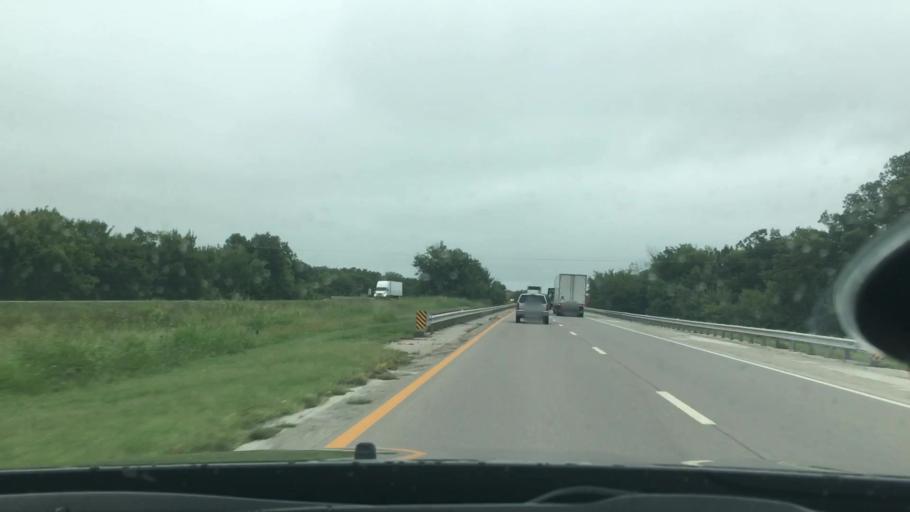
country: US
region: Oklahoma
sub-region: Okfuskee County
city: Okemah
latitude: 35.4283
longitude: -96.2488
